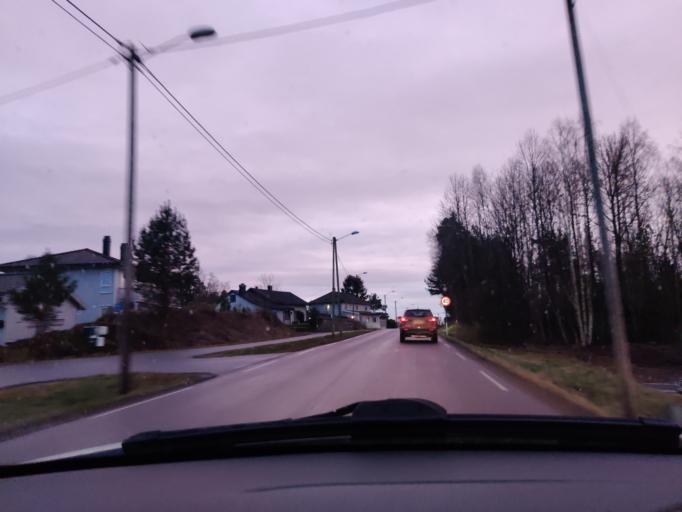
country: NO
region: Vestfold
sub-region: Tonsberg
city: Sem
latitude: 59.2633
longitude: 10.3633
